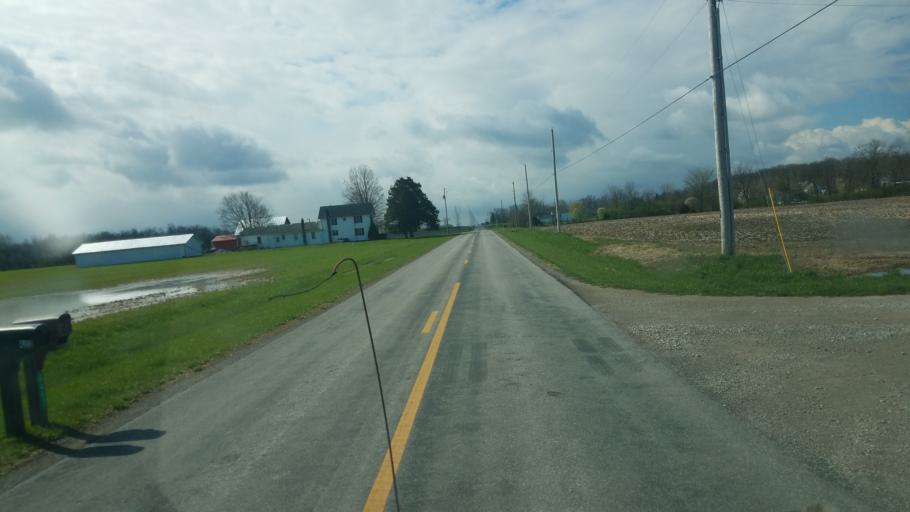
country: US
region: Ohio
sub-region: Delaware County
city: Delaware
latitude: 40.3529
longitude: -83.0211
